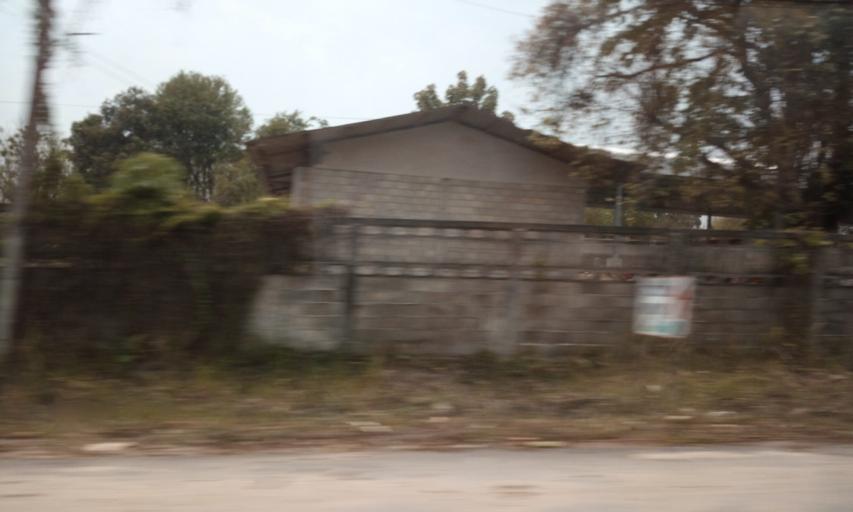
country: TH
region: Phayao
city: Phu Sang
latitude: 19.5926
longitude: 100.3175
